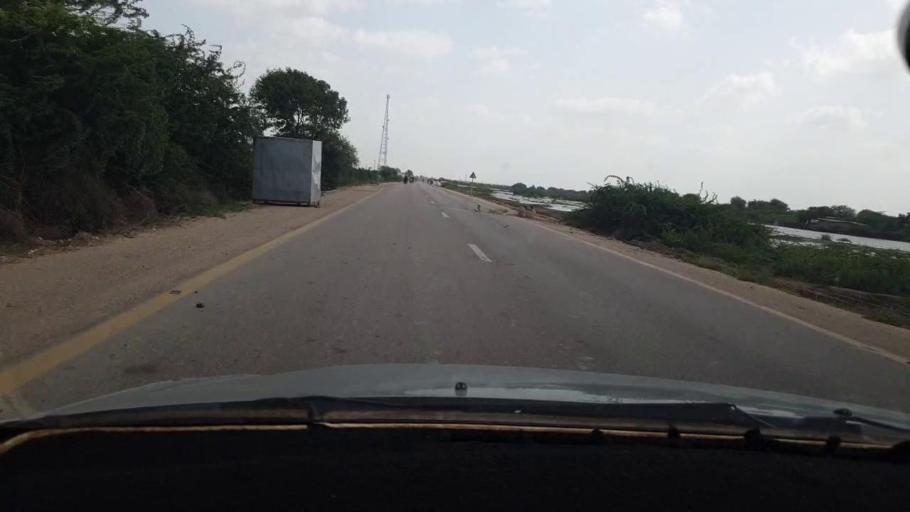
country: PK
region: Sindh
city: Naukot
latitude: 24.9951
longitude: 69.2906
